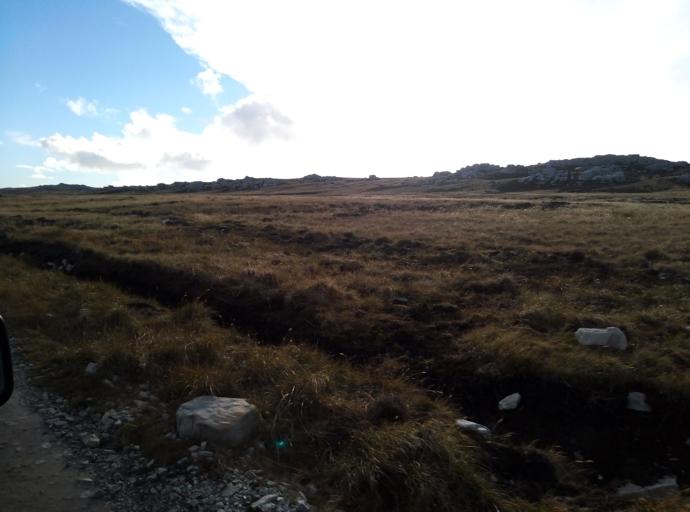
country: FK
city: Stanley
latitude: -51.6843
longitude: -57.9116
